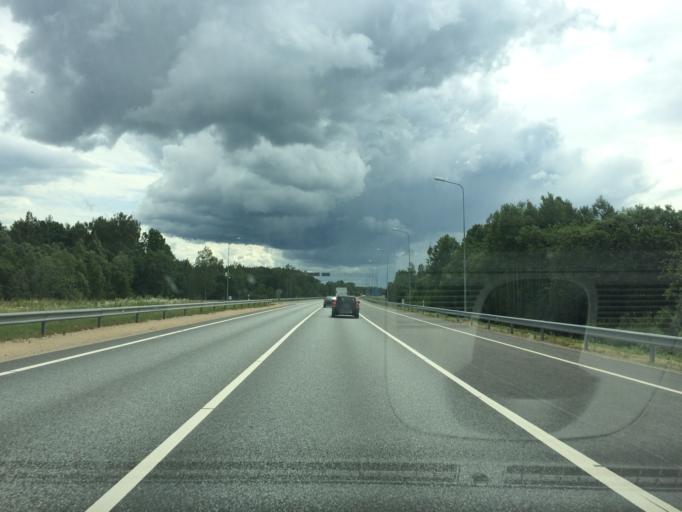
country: LV
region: Skriveri
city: Skriveri
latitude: 56.7656
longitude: 25.0980
